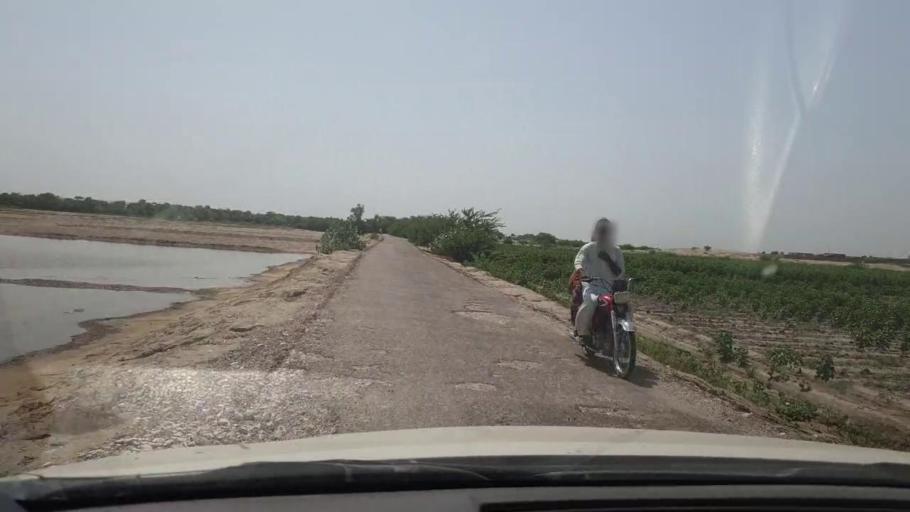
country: PK
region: Sindh
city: Rohri
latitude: 27.5184
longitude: 69.0787
